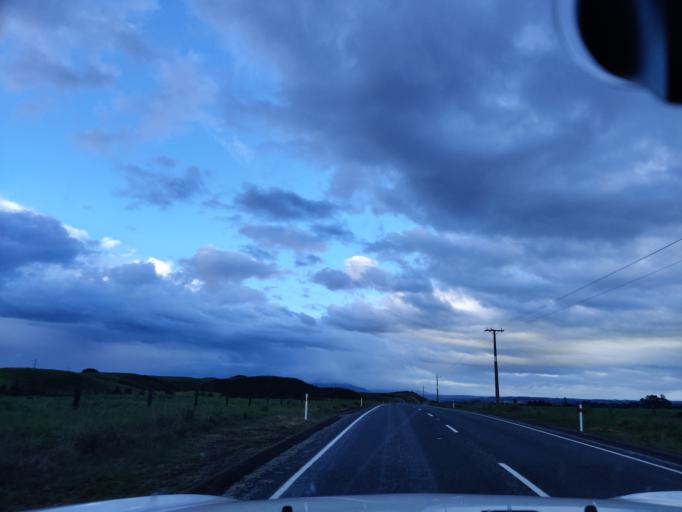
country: NZ
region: Waikato
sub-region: South Waikato District
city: Tokoroa
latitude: -38.3771
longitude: 175.7902
